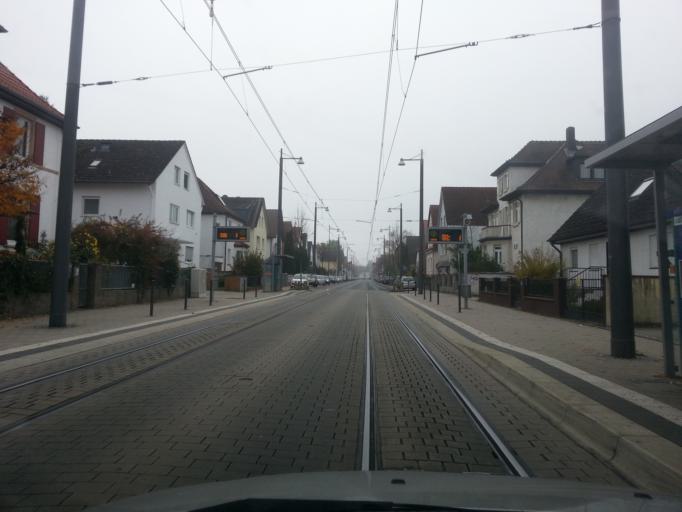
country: DE
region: Hesse
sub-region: Regierungsbezirk Darmstadt
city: Erzhausen
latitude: 49.9179
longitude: 8.6546
